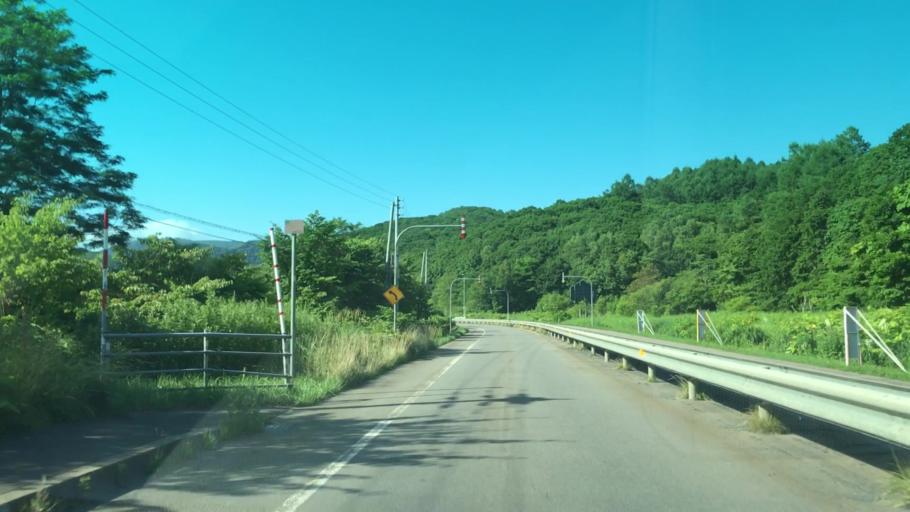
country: JP
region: Hokkaido
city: Iwanai
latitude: 42.9997
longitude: 140.6684
